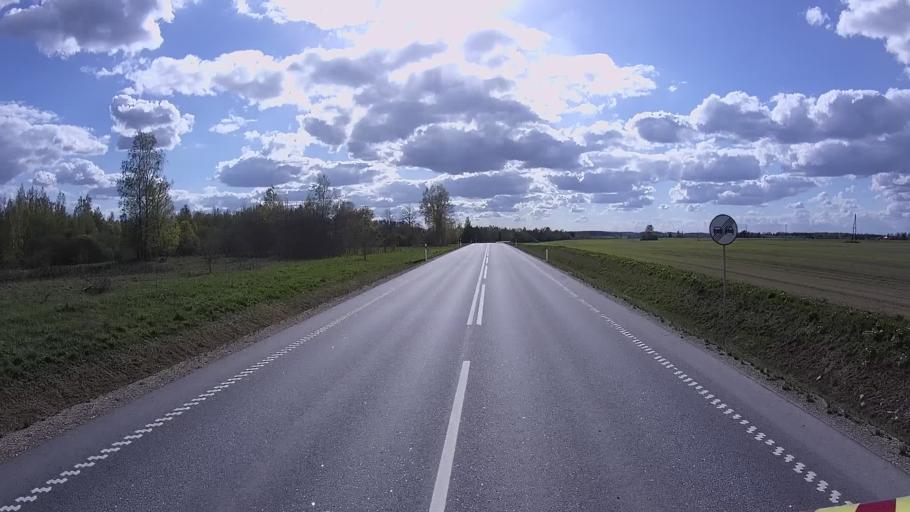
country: EE
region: Jogevamaa
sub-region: Mustvee linn
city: Mustvee
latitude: 58.8330
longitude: 26.7965
